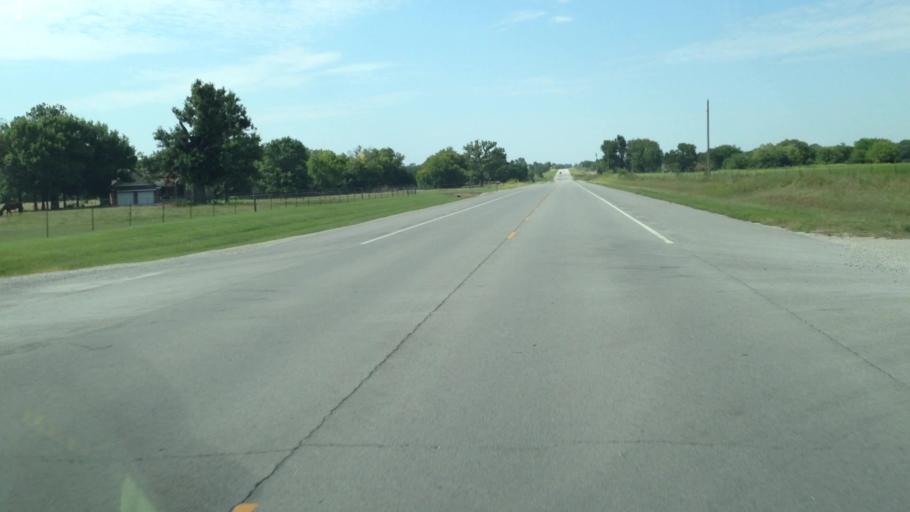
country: US
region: Kansas
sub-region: Labette County
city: Parsons
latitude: 37.2666
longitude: -95.2672
